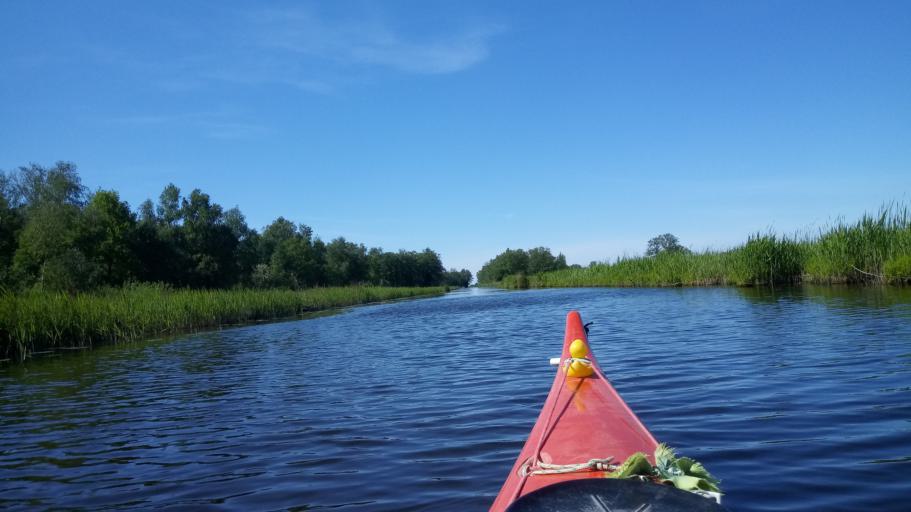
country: NL
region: South Holland
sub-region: Gemeente Nieuwkoop
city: Nieuwkoop
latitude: 52.1458
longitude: 4.8086
